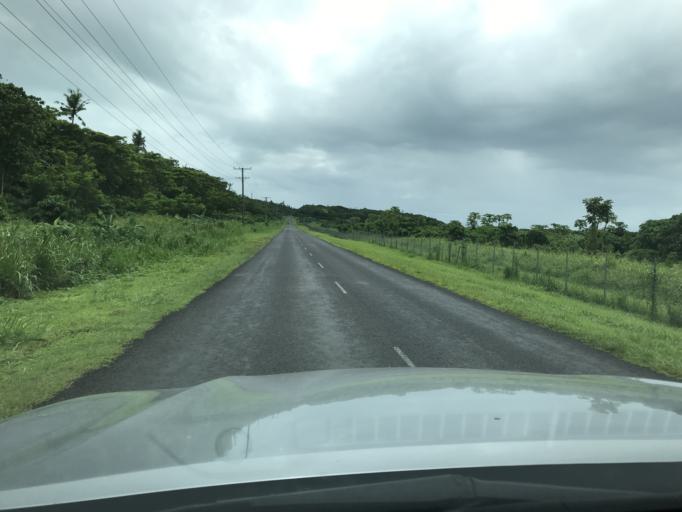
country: WS
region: A'ana
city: Satapuala
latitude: -13.8339
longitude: -172.0077
